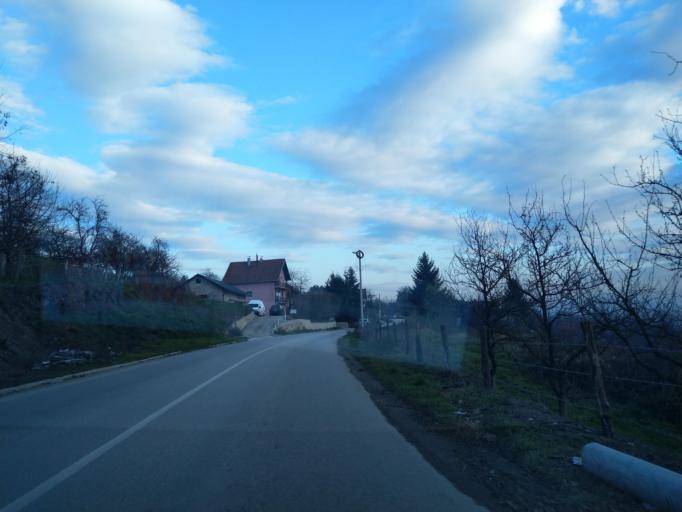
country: RS
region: Central Serbia
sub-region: Zlatiborski Okrug
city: Uzice
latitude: 43.8642
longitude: 19.8906
